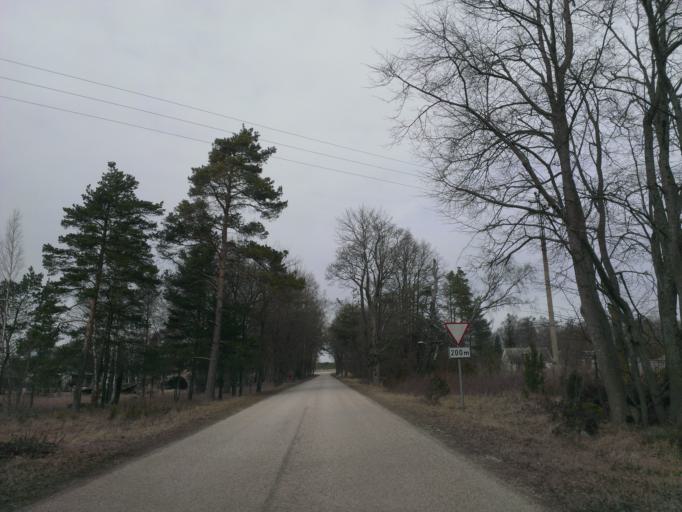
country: EE
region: Laeaene
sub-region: Lihula vald
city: Lihula
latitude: 58.5876
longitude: 23.5373
